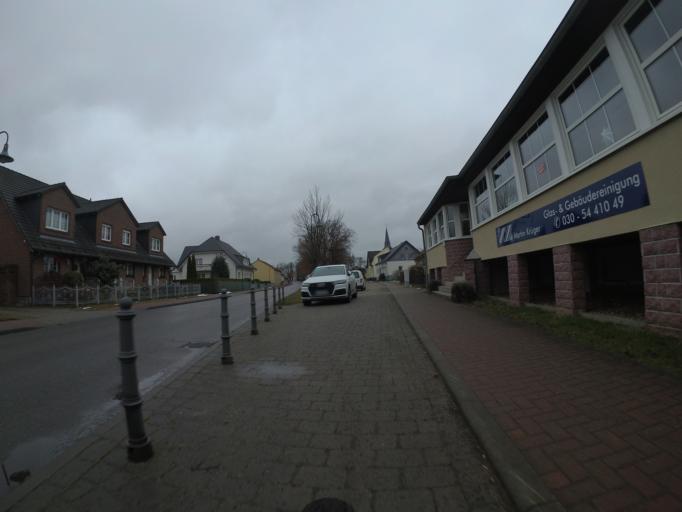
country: DE
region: Brandenburg
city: Ahrensfelde
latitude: 52.5609
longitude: 13.5902
